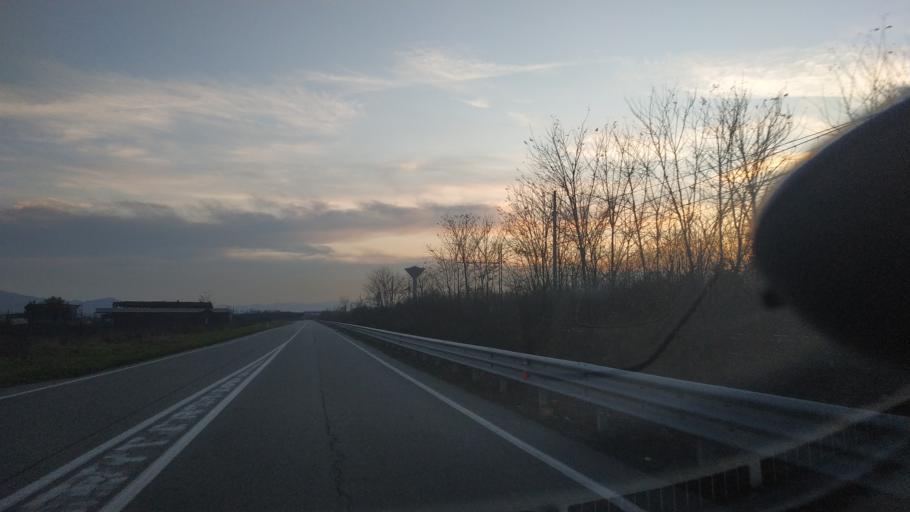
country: IT
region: Piedmont
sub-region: Provincia di Torino
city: Montanaro
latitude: 45.2486
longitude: 7.8642
